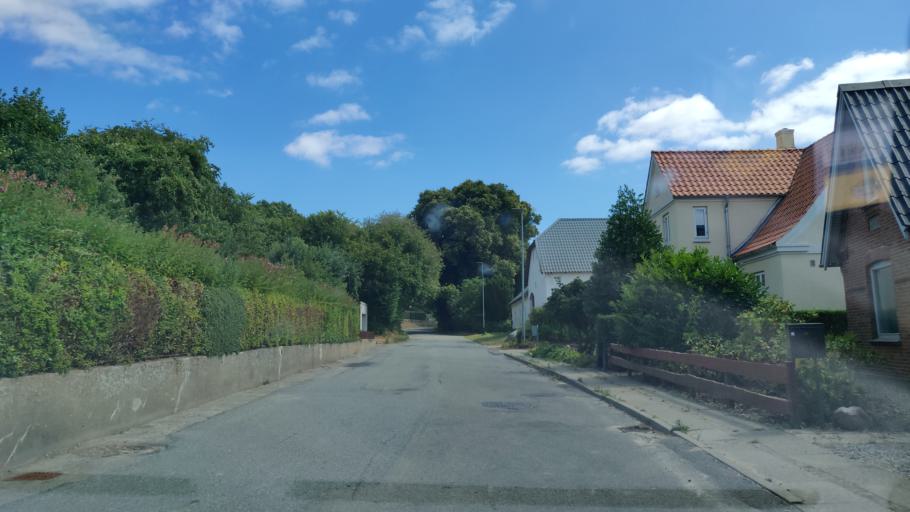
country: DK
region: South Denmark
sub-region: Fredericia Kommune
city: Taulov
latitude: 55.5266
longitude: 9.5408
